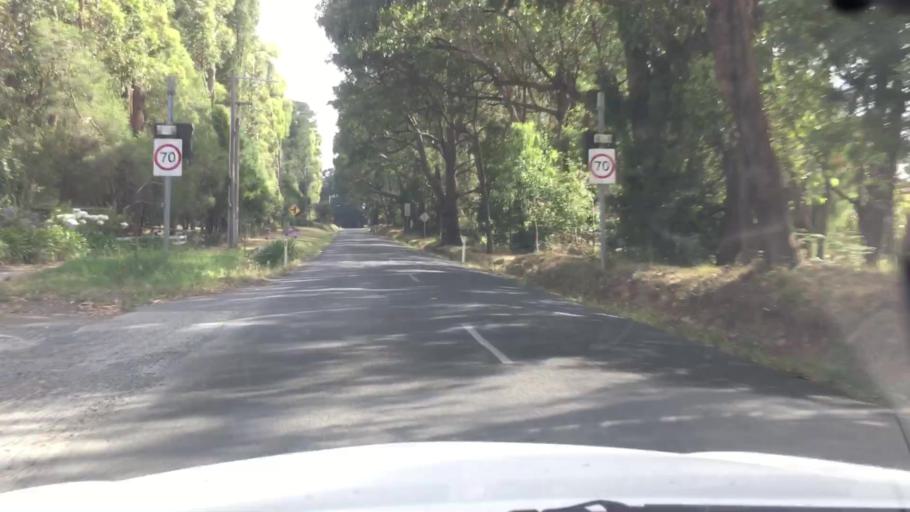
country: AU
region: Victoria
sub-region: Yarra Ranges
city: Macclesfield
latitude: -37.8883
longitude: 145.4760
